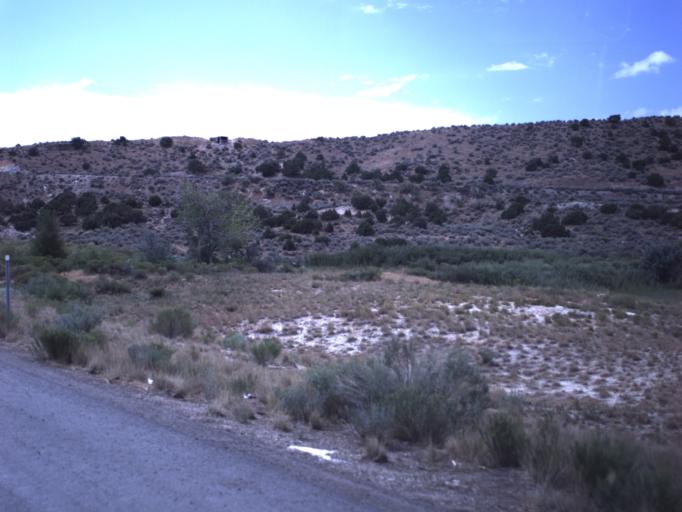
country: US
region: Utah
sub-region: Uintah County
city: Maeser
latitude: 40.4178
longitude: -109.5819
